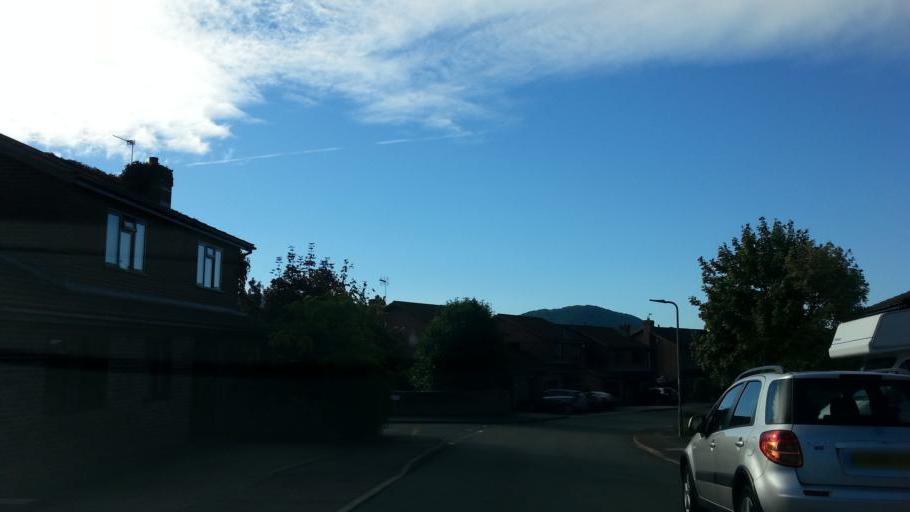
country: GB
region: England
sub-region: Herefordshire
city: Ross on Wye
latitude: 51.9228
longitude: -2.5721
